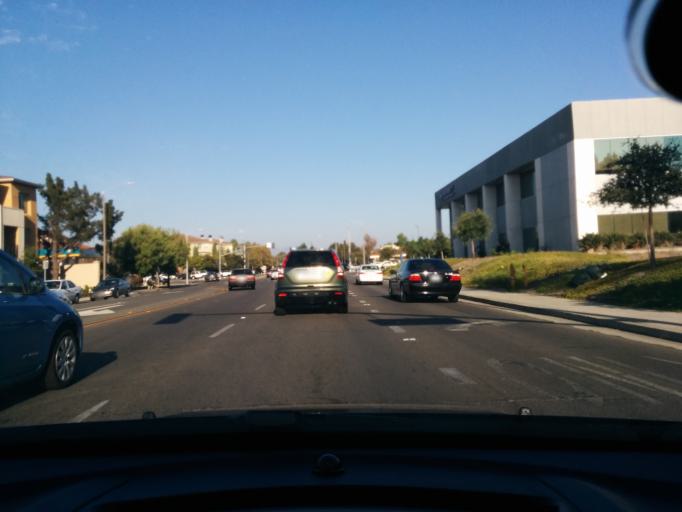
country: US
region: California
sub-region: Santa Clara County
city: Sunnyvale
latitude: 37.3868
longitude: -121.9977
